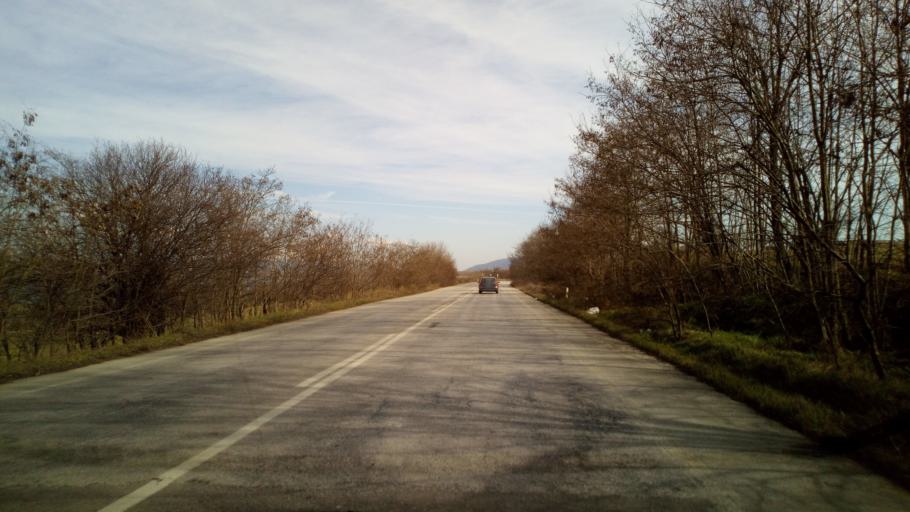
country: GR
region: Central Macedonia
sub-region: Nomos Thessalonikis
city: Agios Vasileios
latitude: 40.6564
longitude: 23.1502
